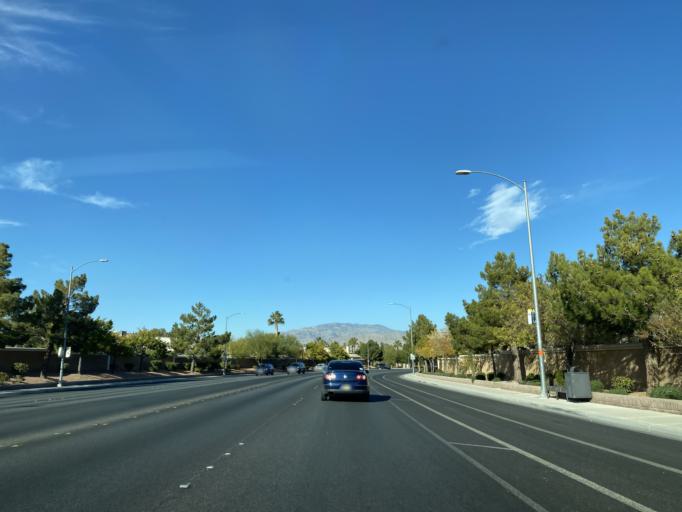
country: US
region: Nevada
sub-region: Clark County
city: Las Vegas
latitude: 36.2909
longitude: -115.2602
